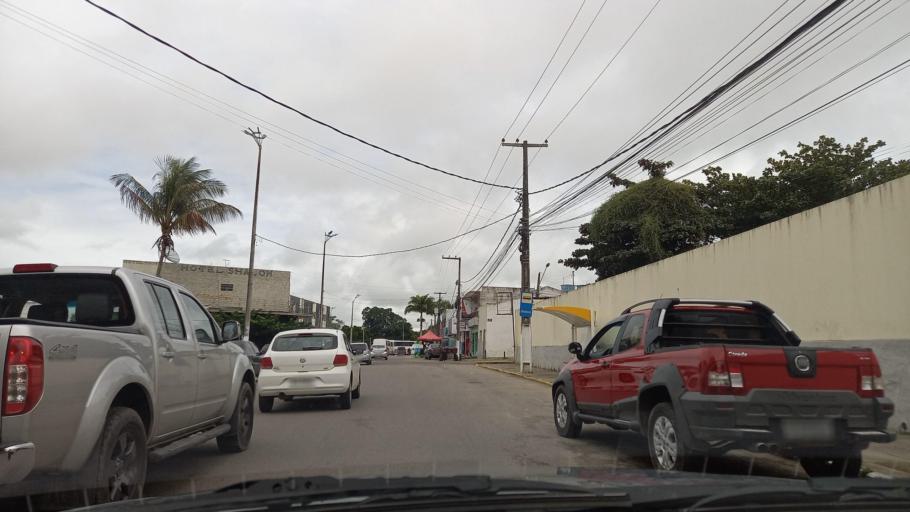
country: BR
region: Pernambuco
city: Garanhuns
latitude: -8.8867
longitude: -36.4906
